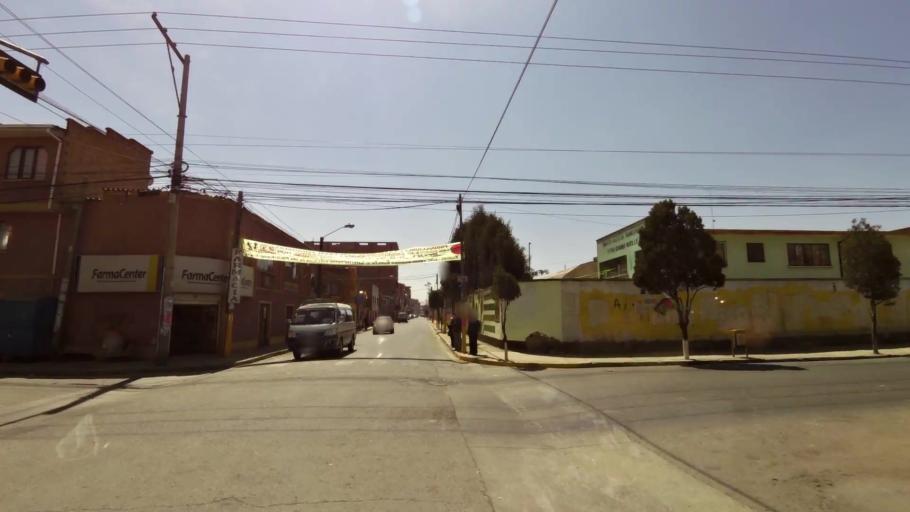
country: BO
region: La Paz
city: La Paz
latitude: -16.5263
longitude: -68.1523
